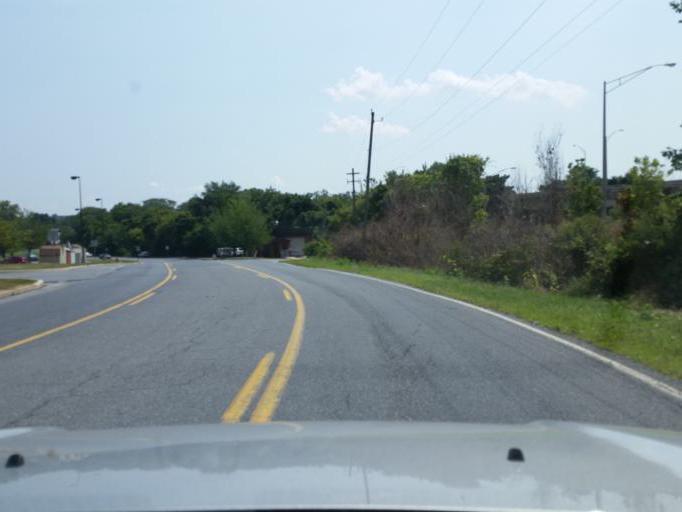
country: US
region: Pennsylvania
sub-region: Dauphin County
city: Lawnton
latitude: 40.2608
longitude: -76.8132
